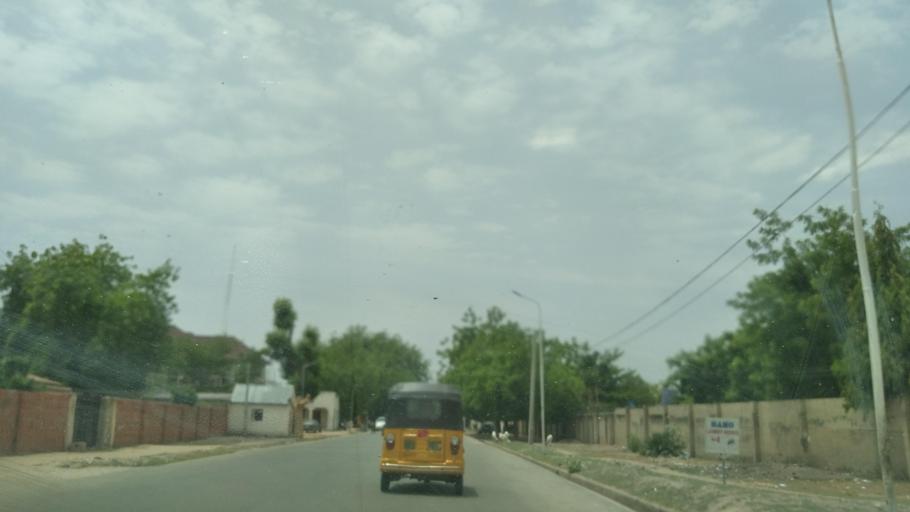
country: NG
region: Borno
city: Maiduguri
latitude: 11.8071
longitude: 13.1582
